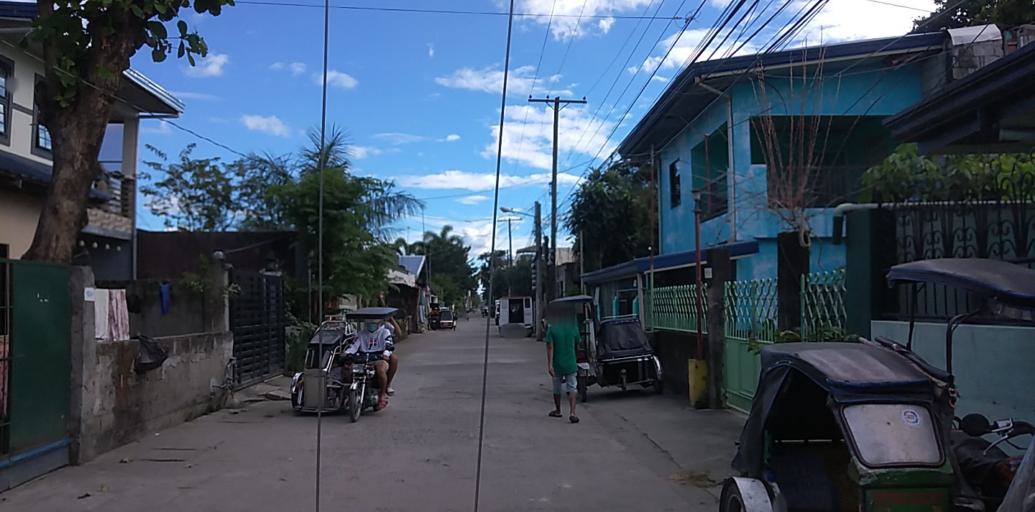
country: PH
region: Central Luzon
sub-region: Province of Pampanga
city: Arayat
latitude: 15.1442
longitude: 120.7678
